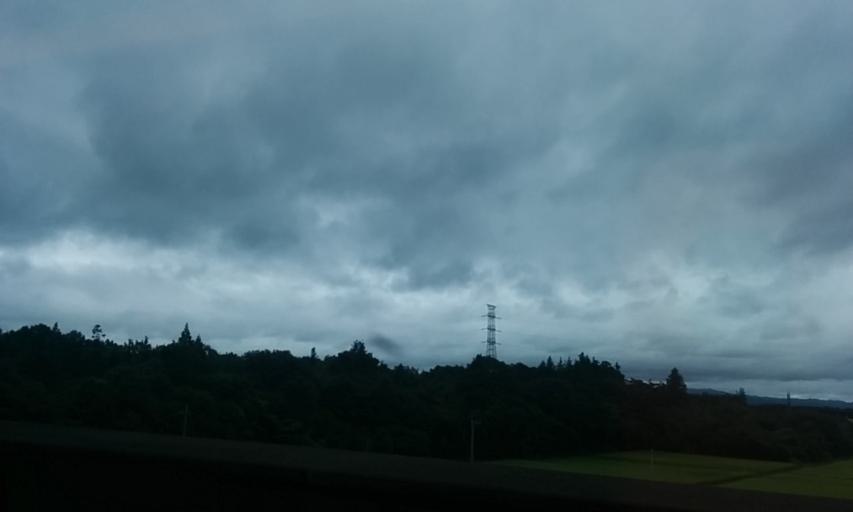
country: JP
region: Tochigi
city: Kuroiso
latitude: 36.9572
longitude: 140.0482
